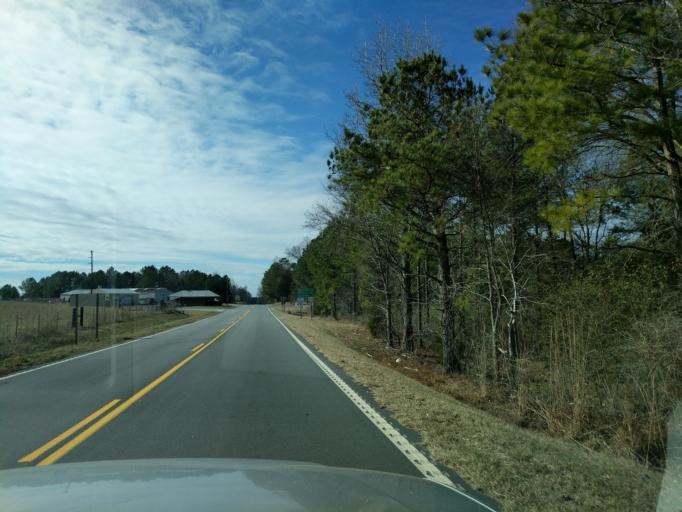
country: US
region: South Carolina
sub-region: Edgefield County
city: Edgefield
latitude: 33.9432
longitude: -81.9256
